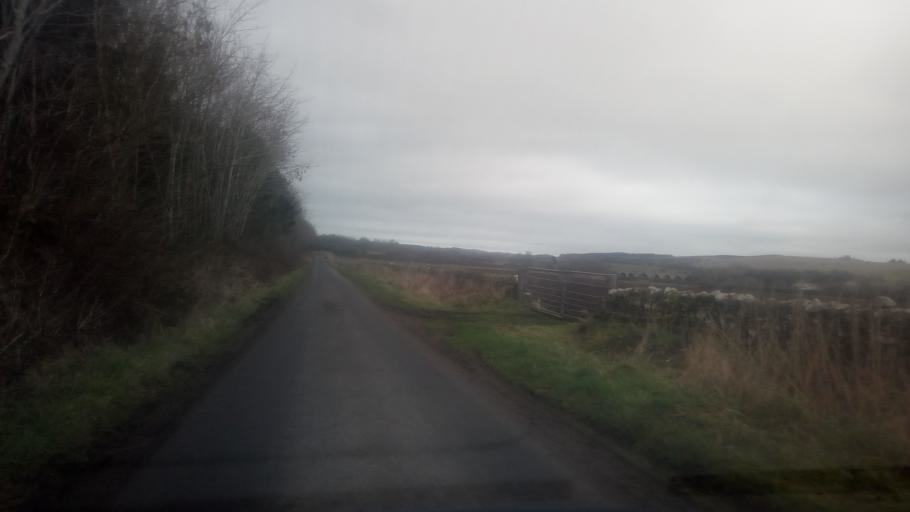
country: GB
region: Scotland
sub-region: The Scottish Borders
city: Kelso
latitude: 55.5609
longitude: -2.4829
